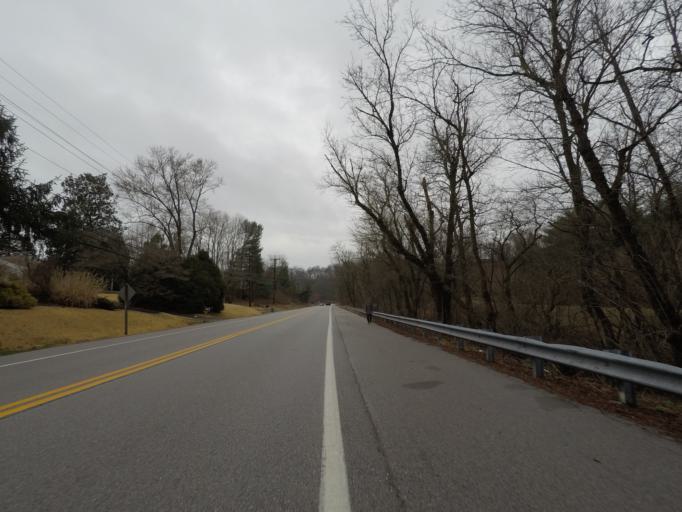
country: US
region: Maryland
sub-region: Howard County
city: Ellicott City
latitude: 39.2731
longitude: -76.8102
